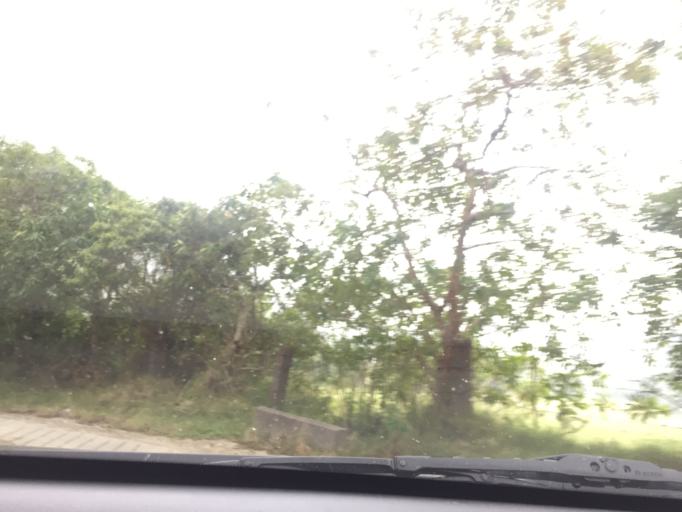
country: CO
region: Cundinamarca
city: Bojaca
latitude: 4.6975
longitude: -74.3693
